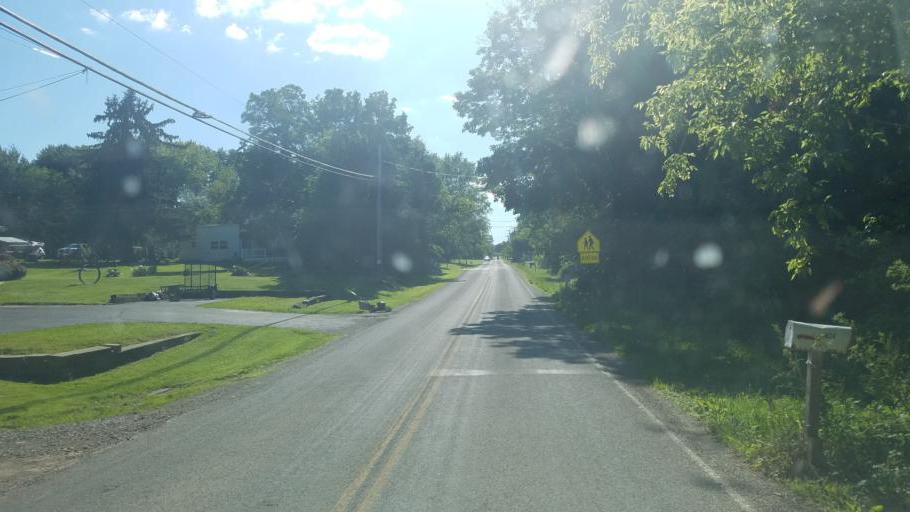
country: US
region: Ohio
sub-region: Richland County
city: Lincoln Heights
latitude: 40.7861
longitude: -82.4477
